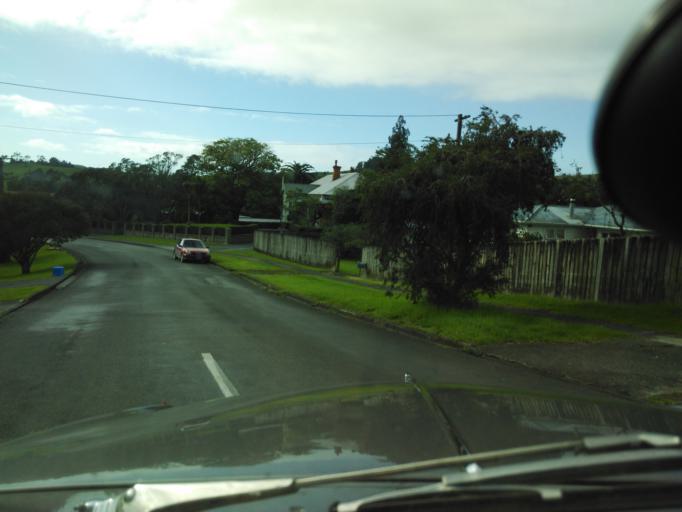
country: NZ
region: Auckland
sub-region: Auckland
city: Wellsford
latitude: -36.2900
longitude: 174.5238
